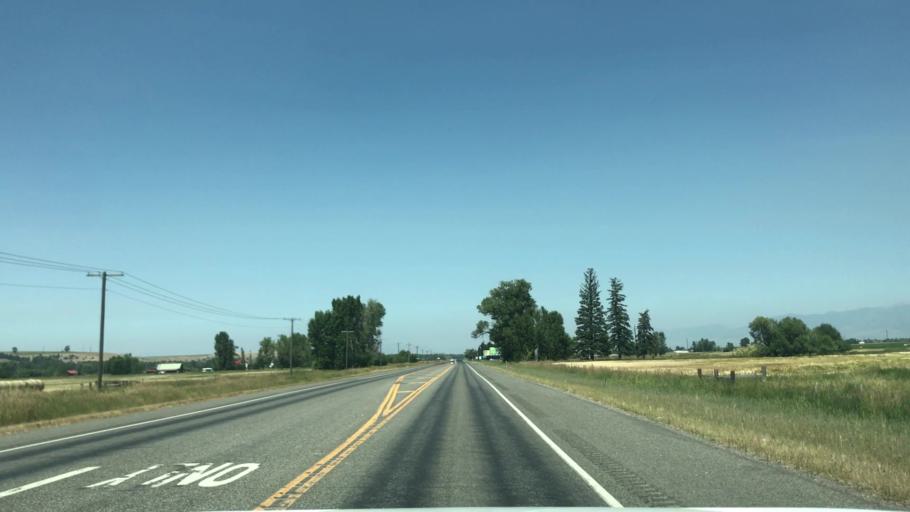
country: US
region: Montana
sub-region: Gallatin County
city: Four Corners
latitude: 45.6198
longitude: -111.1969
